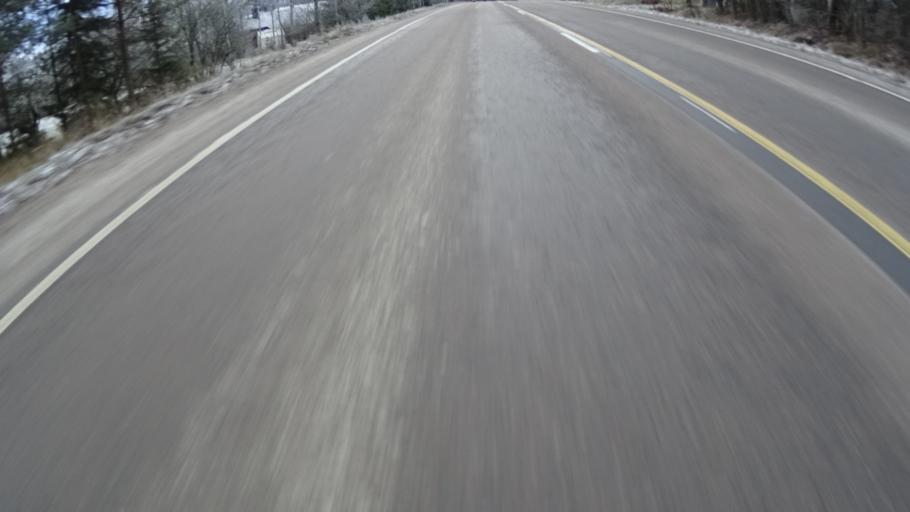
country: FI
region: Uusimaa
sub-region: Helsinki
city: Nurmijaervi
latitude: 60.4024
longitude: 24.7321
